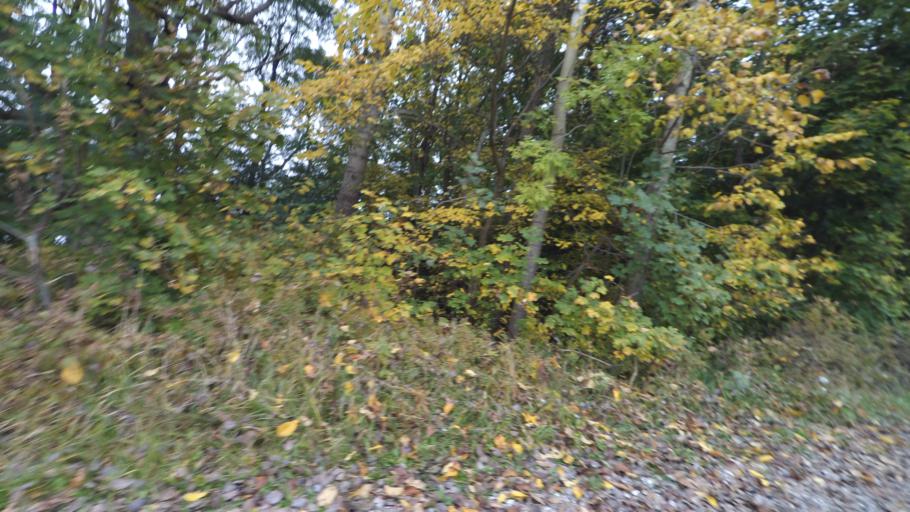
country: DK
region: Central Jutland
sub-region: Arhus Kommune
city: Stavtrup
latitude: 56.1410
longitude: 10.0862
